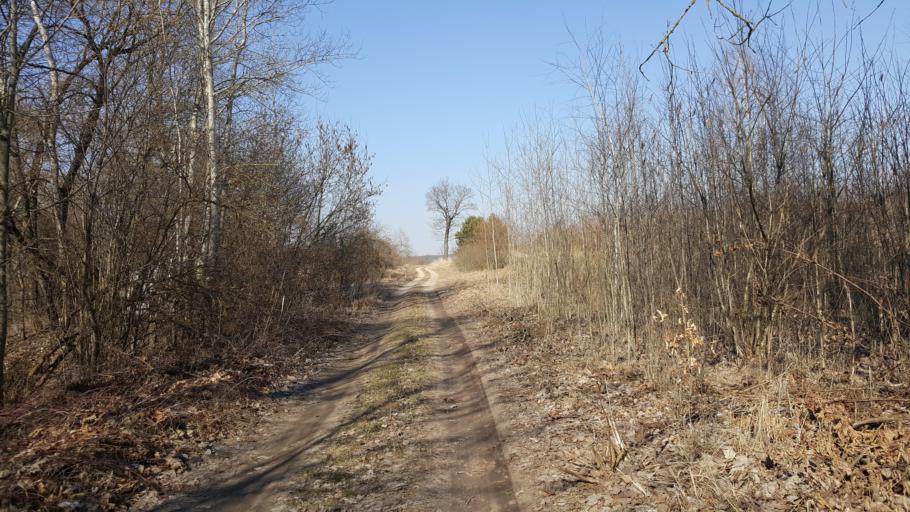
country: BY
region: Brest
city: Kamyanyets
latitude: 52.3640
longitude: 23.7447
